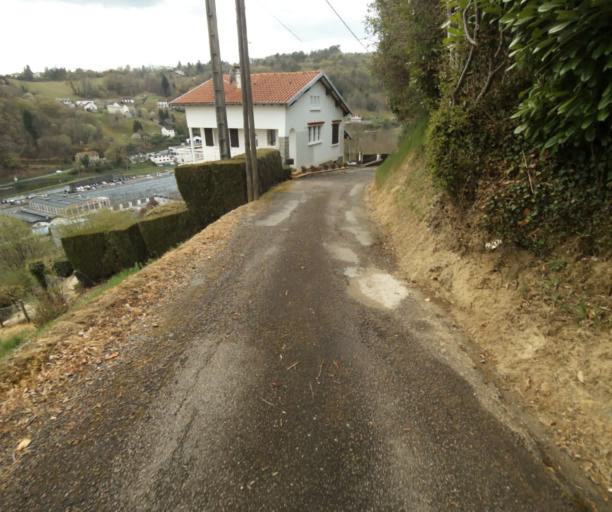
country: FR
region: Limousin
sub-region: Departement de la Correze
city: Tulle
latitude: 45.2628
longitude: 1.7499
